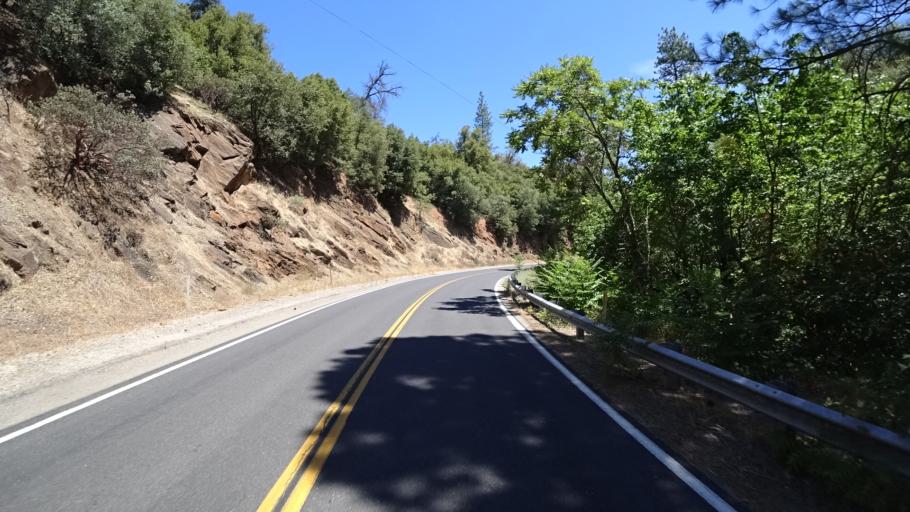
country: US
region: California
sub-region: Calaveras County
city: Murphys
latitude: 38.1346
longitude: -120.4750
